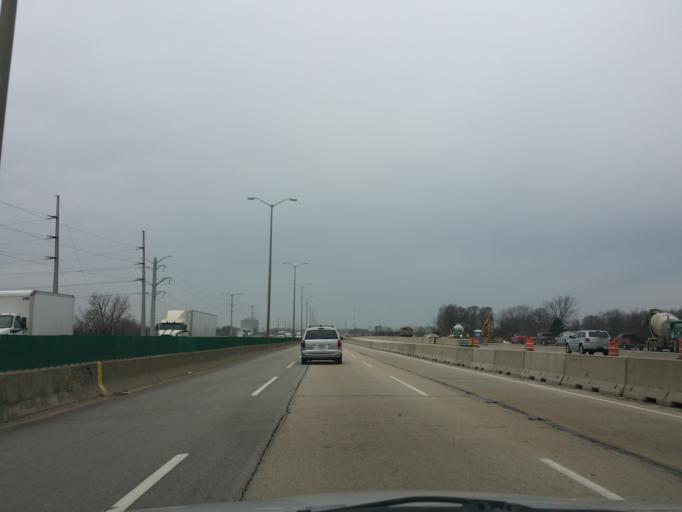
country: US
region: Illinois
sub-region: Cook County
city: Hoffman Estates
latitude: 42.0607
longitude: -88.0531
